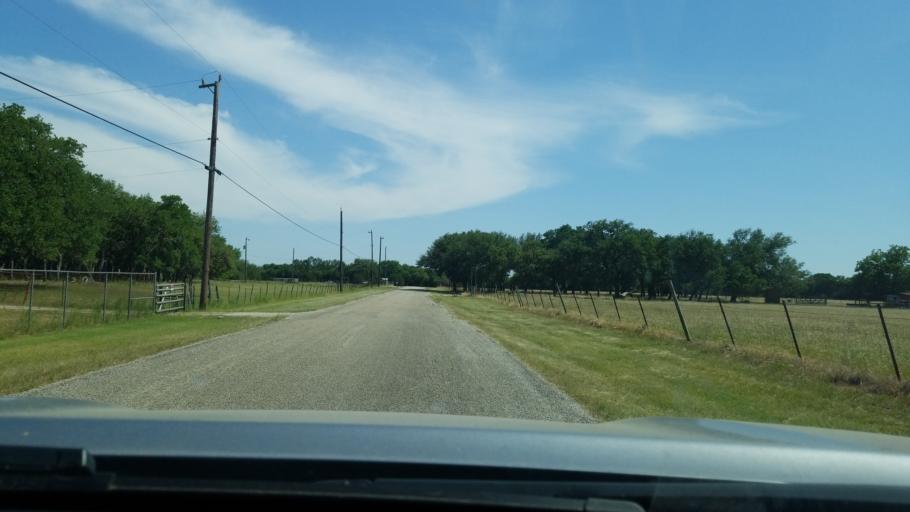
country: US
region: Texas
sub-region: Bexar County
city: Timberwood Park
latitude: 29.7478
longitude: -98.5154
